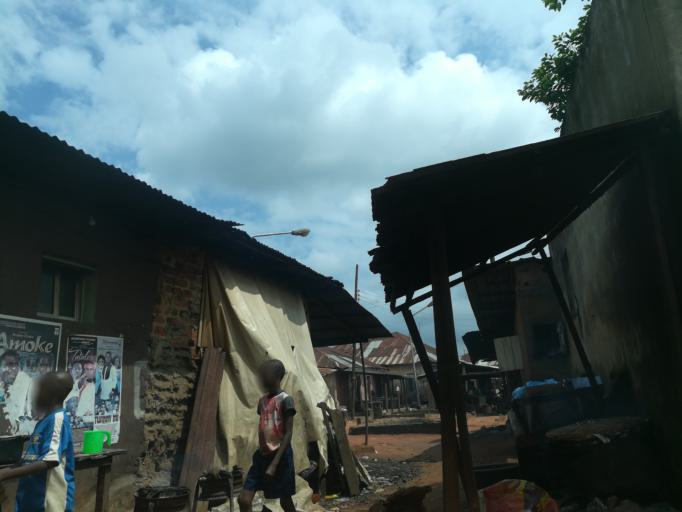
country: NG
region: Lagos
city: Ejirin
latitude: 6.6437
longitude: 3.7133
